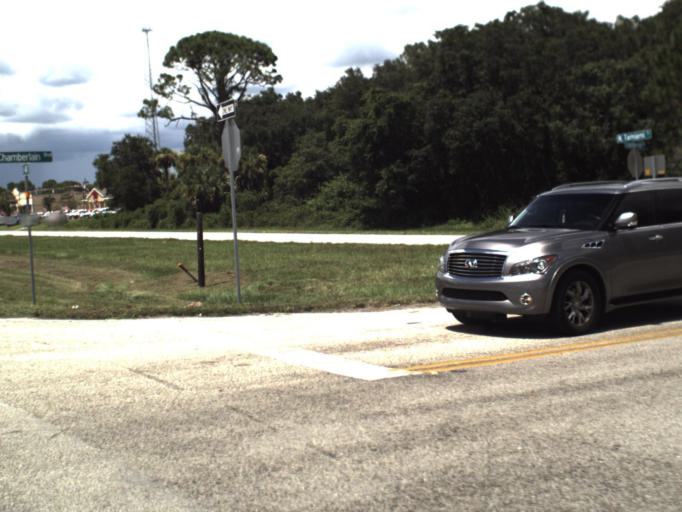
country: US
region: Florida
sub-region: Sarasota County
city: North Port
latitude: 27.0199
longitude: -82.1863
